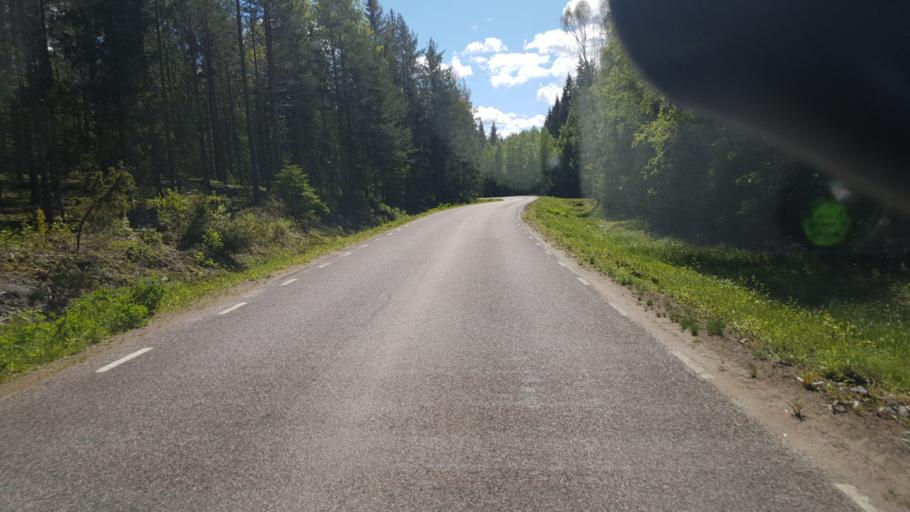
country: SE
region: Vaermland
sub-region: Arvika Kommun
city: Arvika
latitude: 59.5156
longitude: 12.8520
